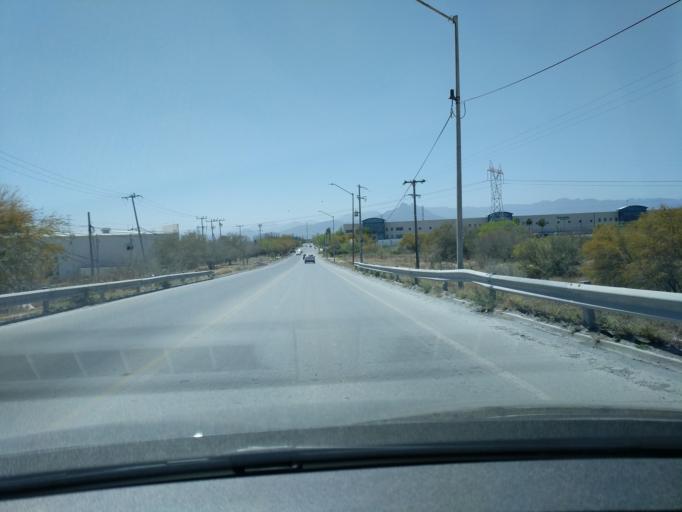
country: MX
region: Nuevo Leon
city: Apodaca
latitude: 25.7928
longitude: -100.1578
